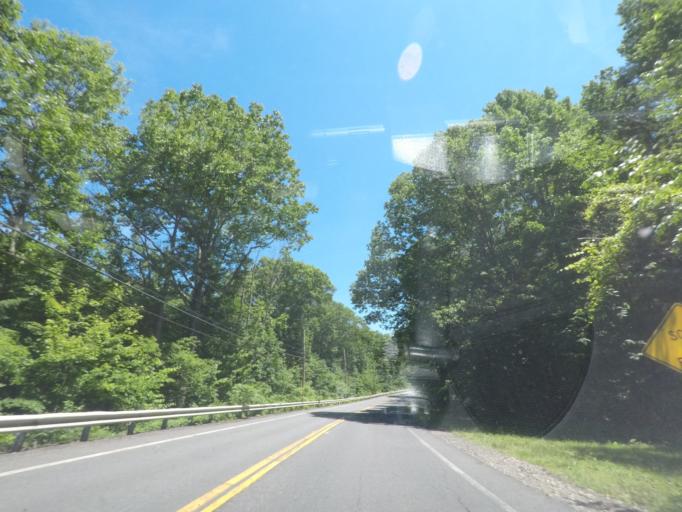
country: US
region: Massachusetts
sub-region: Berkshire County
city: Becket
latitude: 42.2574
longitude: -72.9368
